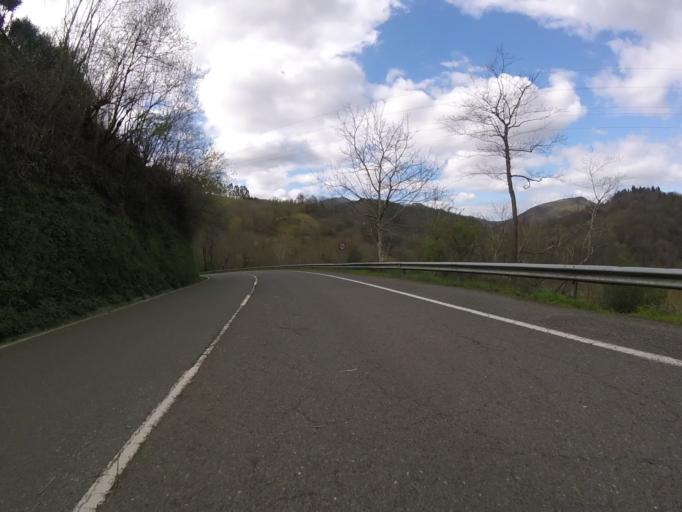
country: ES
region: Navarre
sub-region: Provincia de Navarra
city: Arano
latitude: 43.2208
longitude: -1.9121
